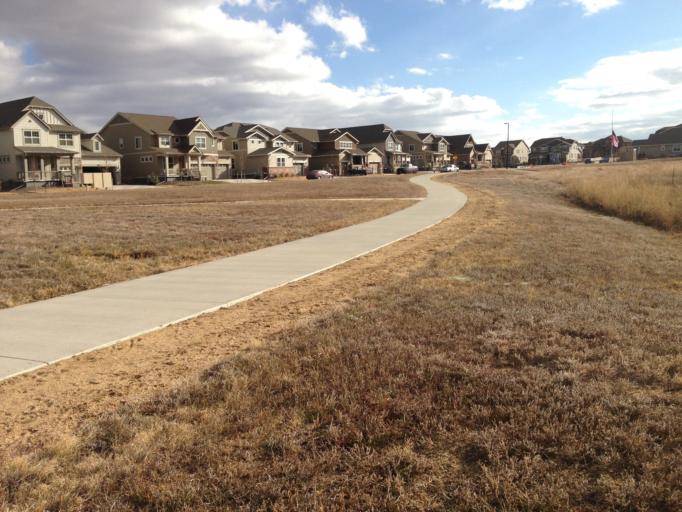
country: US
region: Colorado
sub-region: Boulder County
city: Lafayette
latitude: 40.0319
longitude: -105.0903
